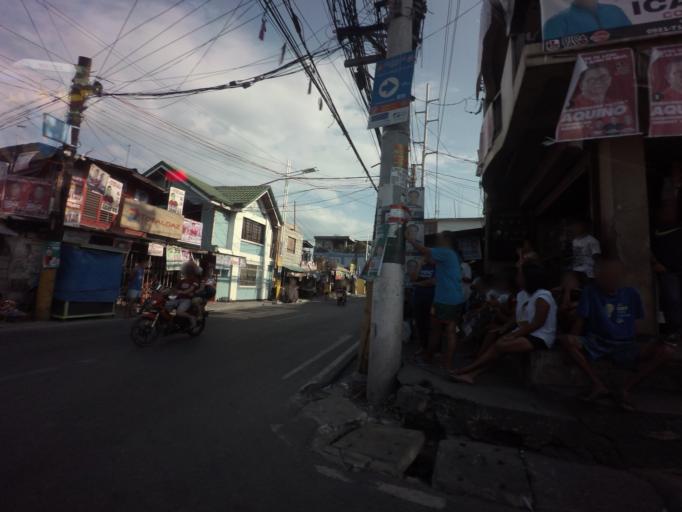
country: PH
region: Calabarzon
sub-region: Province of Rizal
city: Taguig
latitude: 14.4782
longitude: 121.0607
